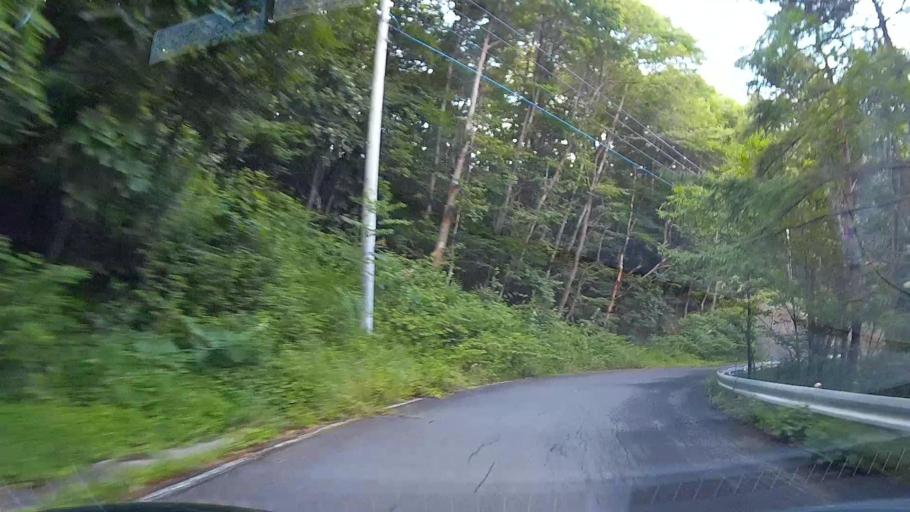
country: JP
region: Gunma
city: Nakanojomachi
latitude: 36.6279
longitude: 138.6249
